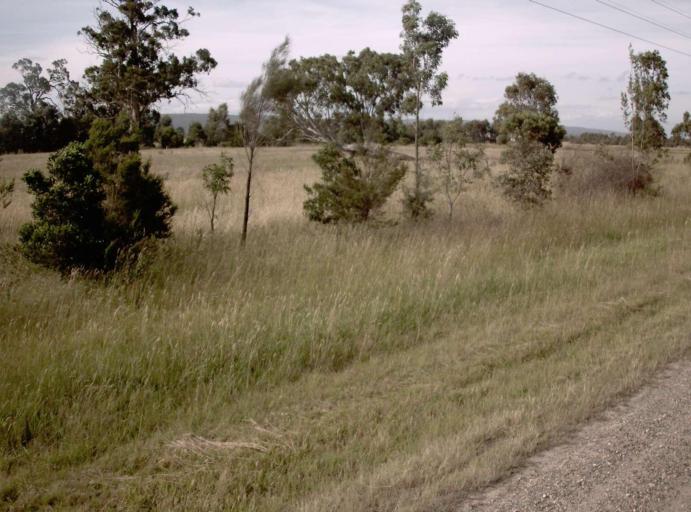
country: AU
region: Victoria
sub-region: Latrobe
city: Traralgon
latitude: -38.1179
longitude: 146.5772
